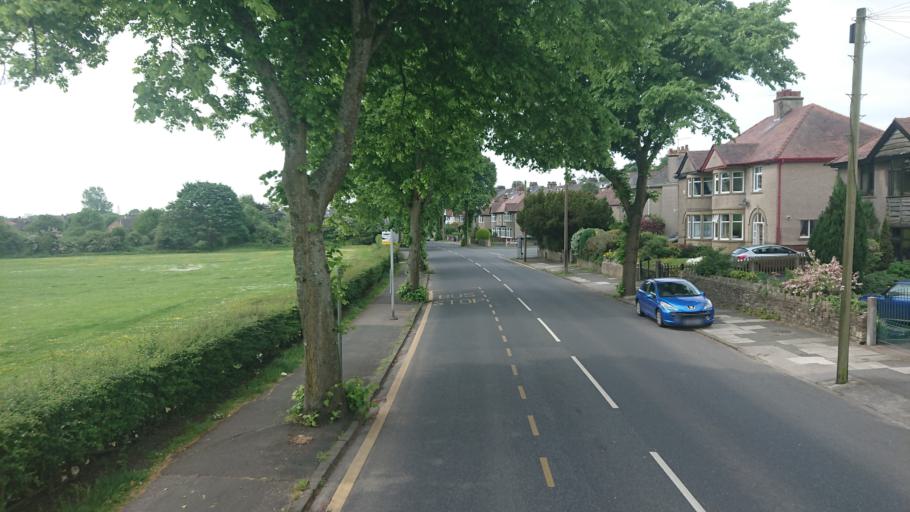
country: GB
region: England
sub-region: Lancashire
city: Lancaster
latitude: 54.0318
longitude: -2.7914
